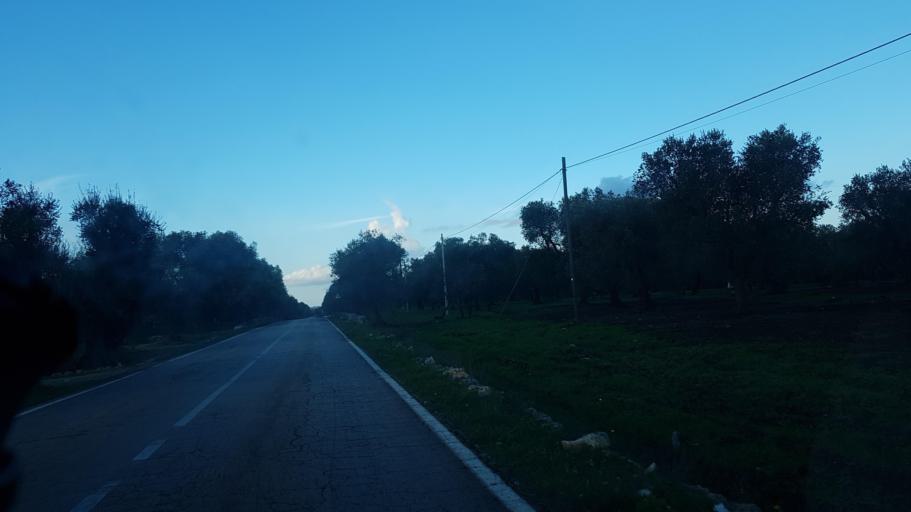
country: IT
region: Apulia
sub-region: Provincia di Brindisi
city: San Michele Salentino
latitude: 40.6478
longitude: 17.6069
